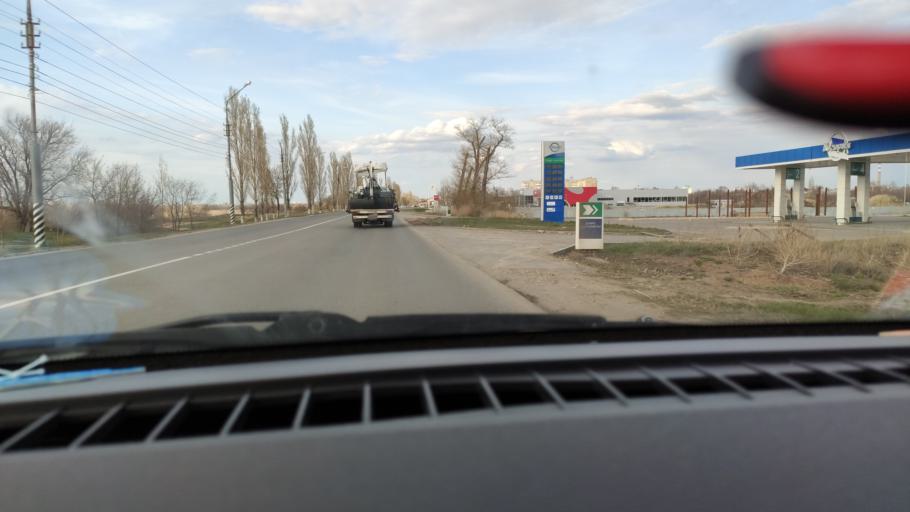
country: RU
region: Saratov
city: Privolzhskiy
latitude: 51.4437
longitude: 46.0719
